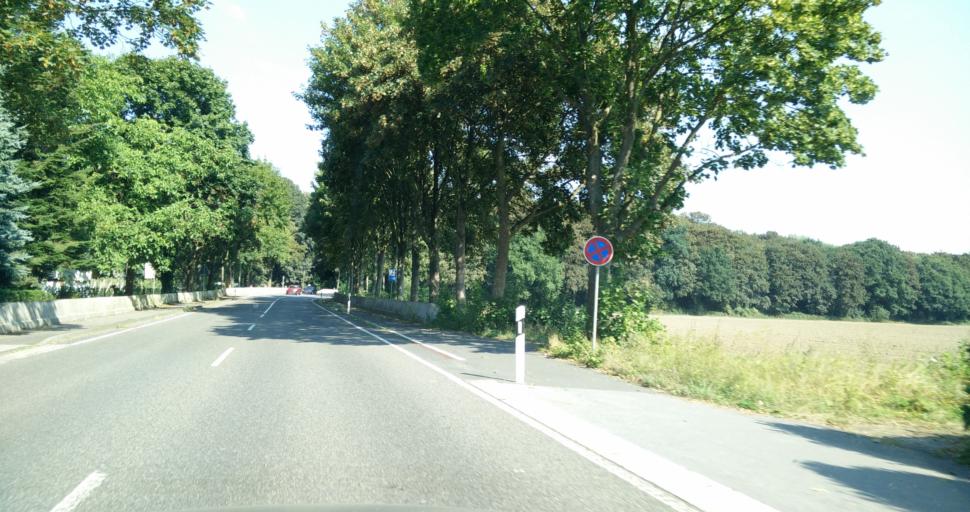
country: DE
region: North Rhine-Westphalia
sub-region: Regierungsbezirk Dusseldorf
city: Hochfeld
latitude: 51.3460
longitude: 6.7425
